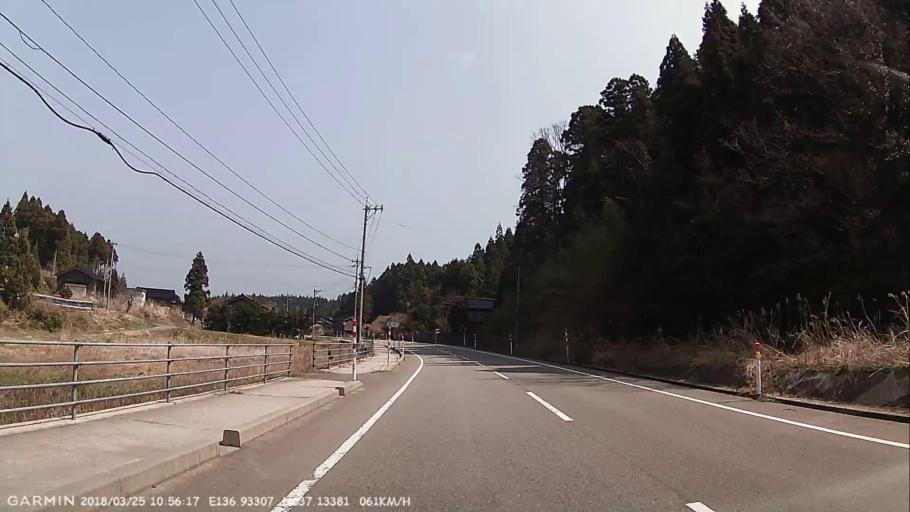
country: JP
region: Ishikawa
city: Nanao
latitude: 37.1339
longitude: 136.9332
